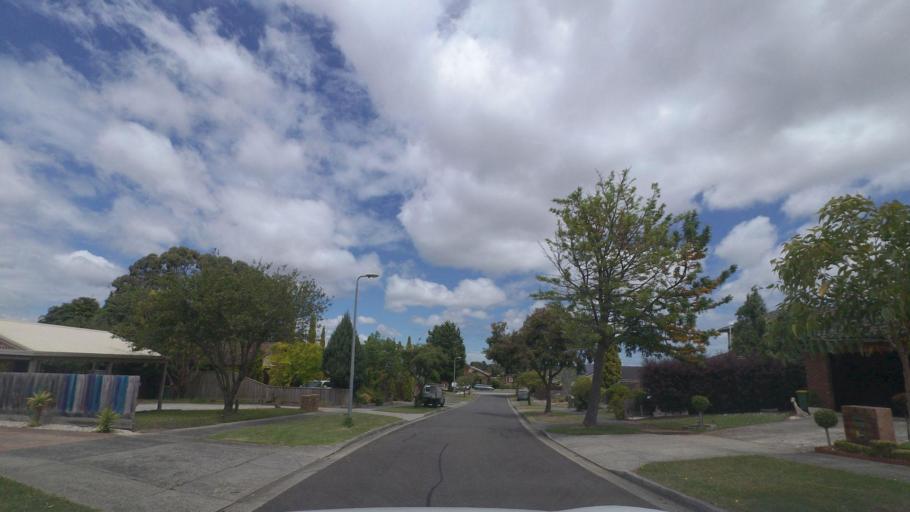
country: AU
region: Victoria
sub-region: Knox
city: Knoxfield
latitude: -37.9076
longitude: 145.2635
